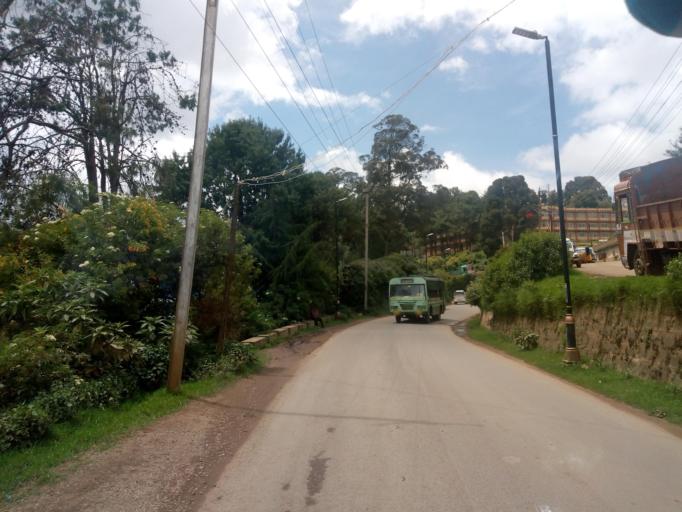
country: IN
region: Tamil Nadu
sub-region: Nilgiri
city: Ooty
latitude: 11.4021
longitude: 76.6974
